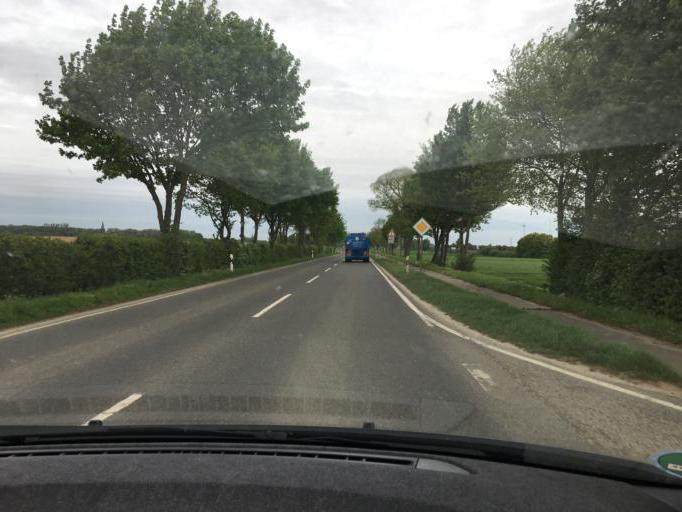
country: DE
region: North Rhine-Westphalia
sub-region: Regierungsbezirk Koln
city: Titz
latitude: 51.0748
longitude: 6.4253
